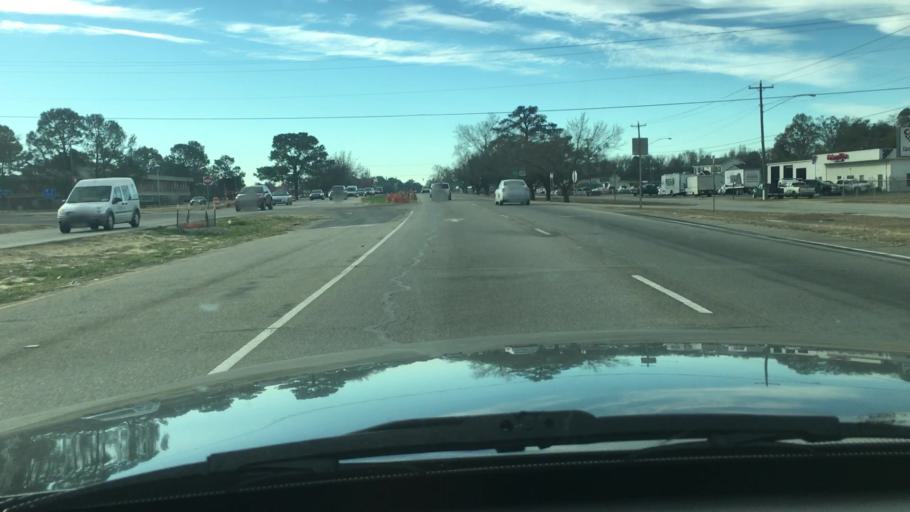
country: US
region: North Carolina
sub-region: Cumberland County
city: Fayetteville
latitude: 35.0159
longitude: -78.8969
